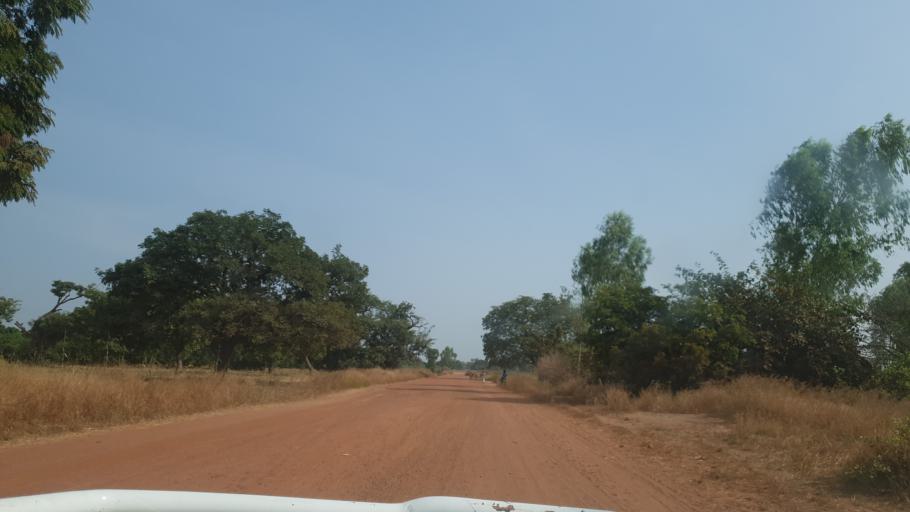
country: ML
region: Koulikoro
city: Dioila
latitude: 12.2262
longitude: -6.2156
